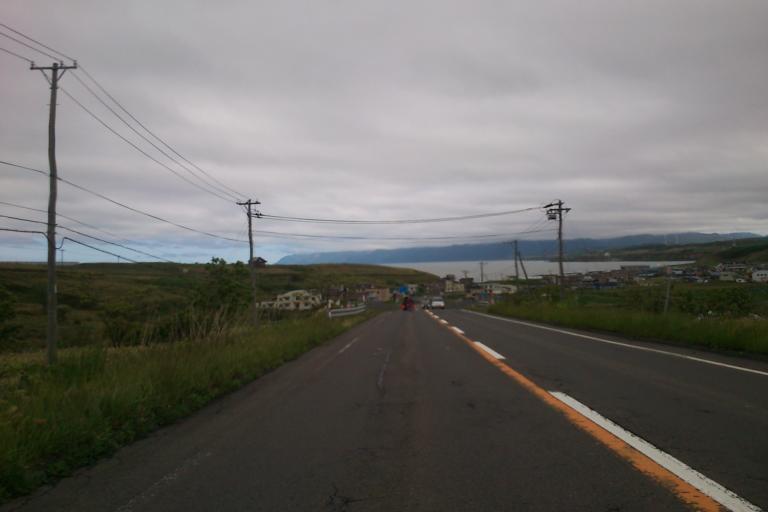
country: JP
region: Hokkaido
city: Ishikari
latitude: 43.3079
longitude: 141.4123
